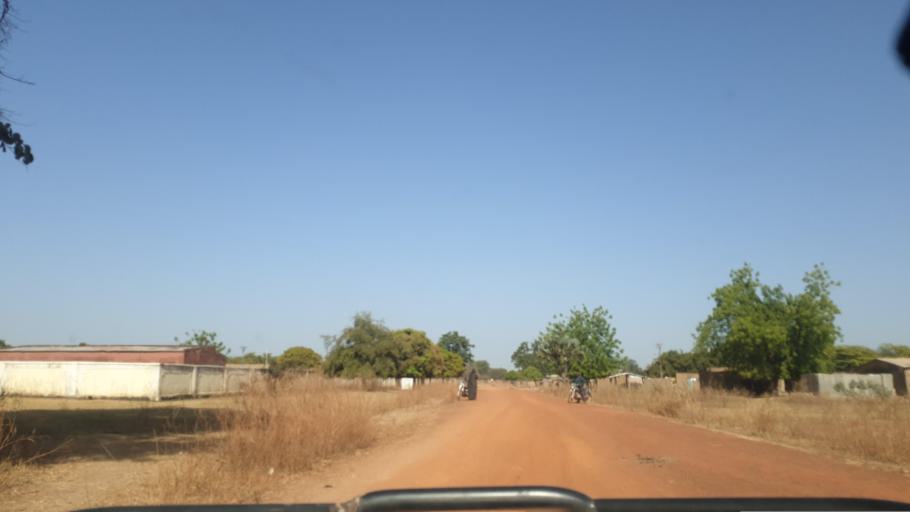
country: ML
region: Sikasso
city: Bougouni
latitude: 11.8122
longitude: -6.9345
